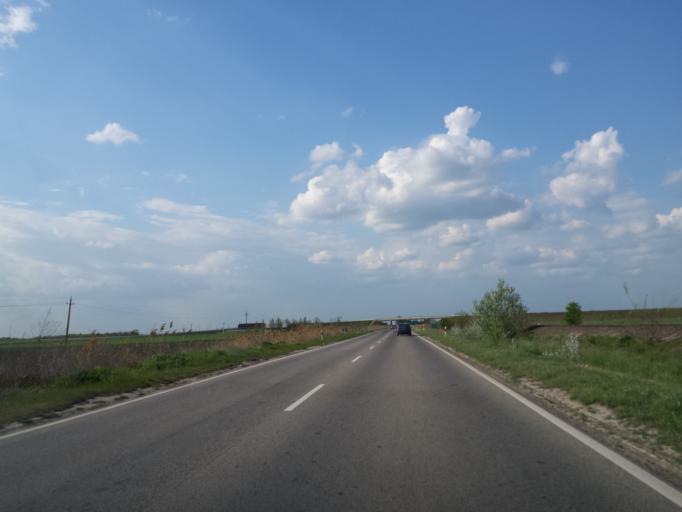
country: HU
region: Csongrad
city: Mako
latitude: 46.2611
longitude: 20.4833
